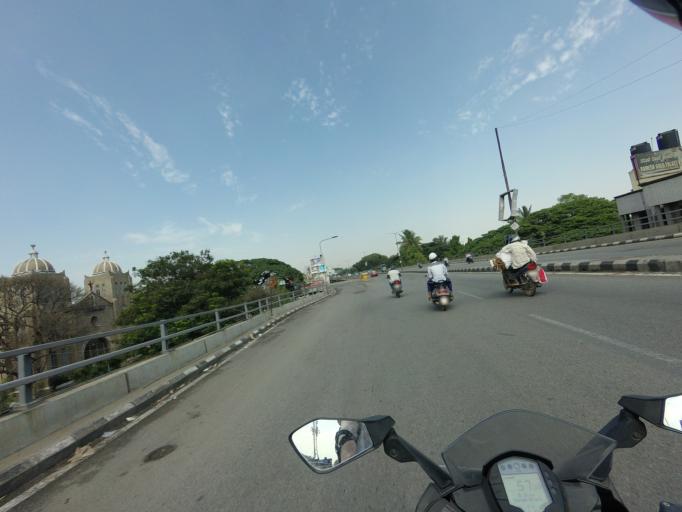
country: IN
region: Karnataka
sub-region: Bangalore Urban
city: Bangalore
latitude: 12.9642
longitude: 77.5704
